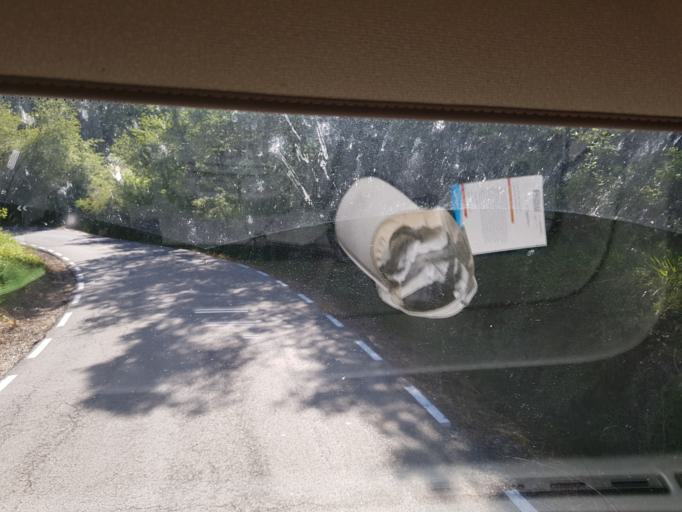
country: ES
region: Castille and Leon
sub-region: Provincia de Burgos
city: Espinosa de los Monteros
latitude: 43.1253
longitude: -3.5811
